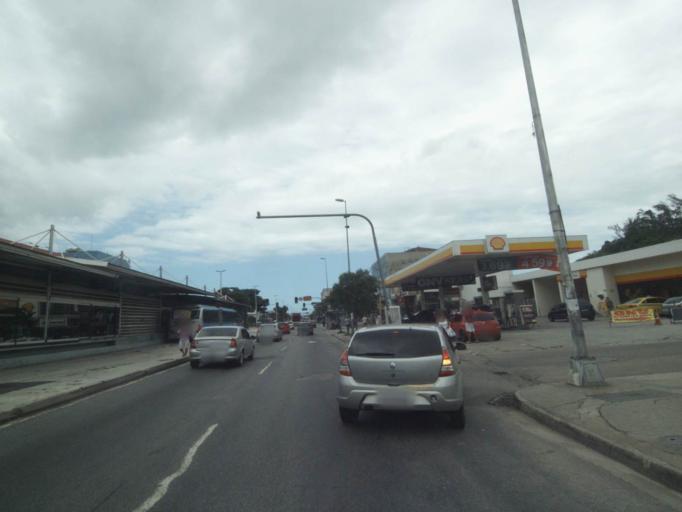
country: BR
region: Rio de Janeiro
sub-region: Sao Joao De Meriti
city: Sao Joao de Meriti
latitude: -22.9243
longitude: -43.3740
